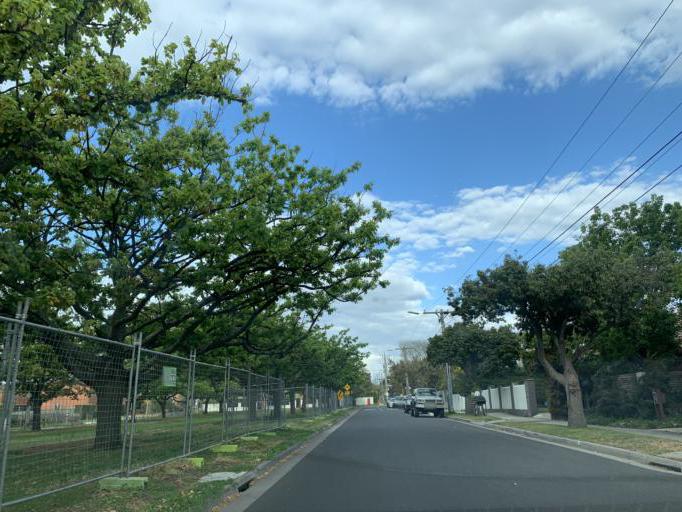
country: AU
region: Victoria
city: Hampton
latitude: -37.9478
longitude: 145.0123
